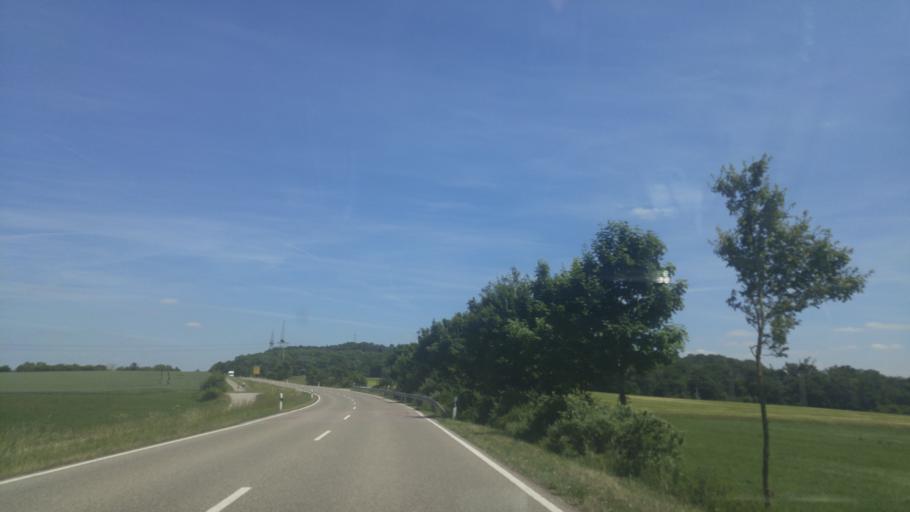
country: DE
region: Bavaria
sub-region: Regierungsbezirk Mittelfranken
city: Steinsfeld
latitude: 49.4405
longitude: 10.2204
